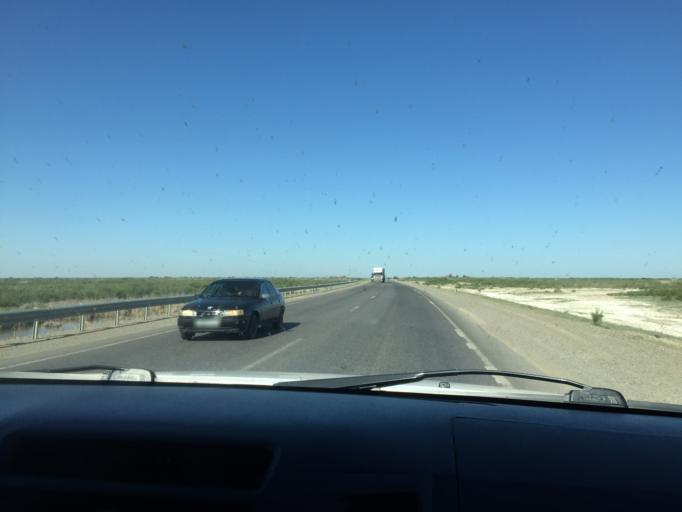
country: KZ
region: Qyzylorda
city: Terenozek
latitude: 44.8863
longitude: 65.1683
